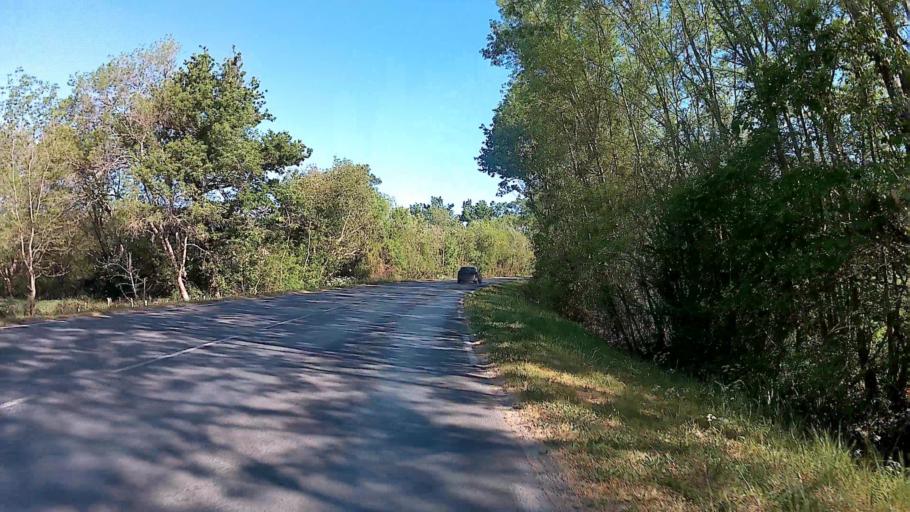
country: FR
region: Aquitaine
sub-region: Departement de la Gironde
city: Cadaujac
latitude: 44.7617
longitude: -0.5292
